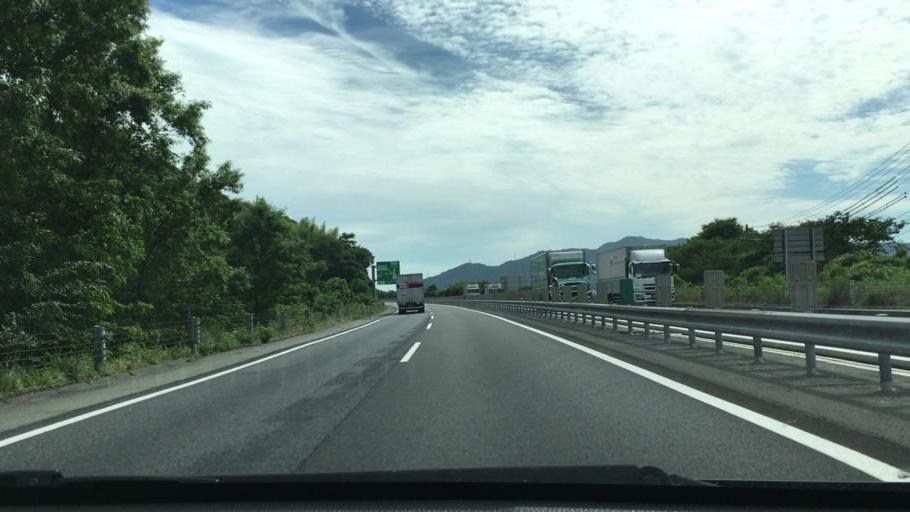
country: JP
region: Yamaguchi
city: Ogori-shimogo
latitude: 34.1314
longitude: 131.4254
